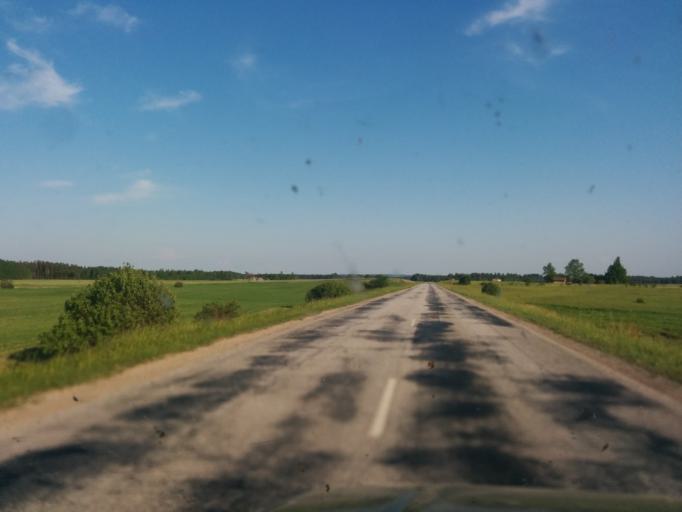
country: LV
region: Talsu Rajons
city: Valdemarpils
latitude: 57.3229
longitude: 22.5260
